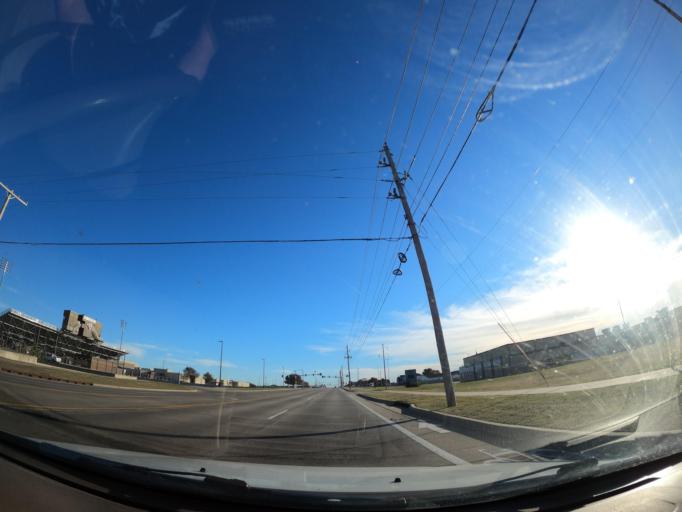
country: US
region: Oklahoma
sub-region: Tulsa County
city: Owasso
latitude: 36.2823
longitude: -95.8303
